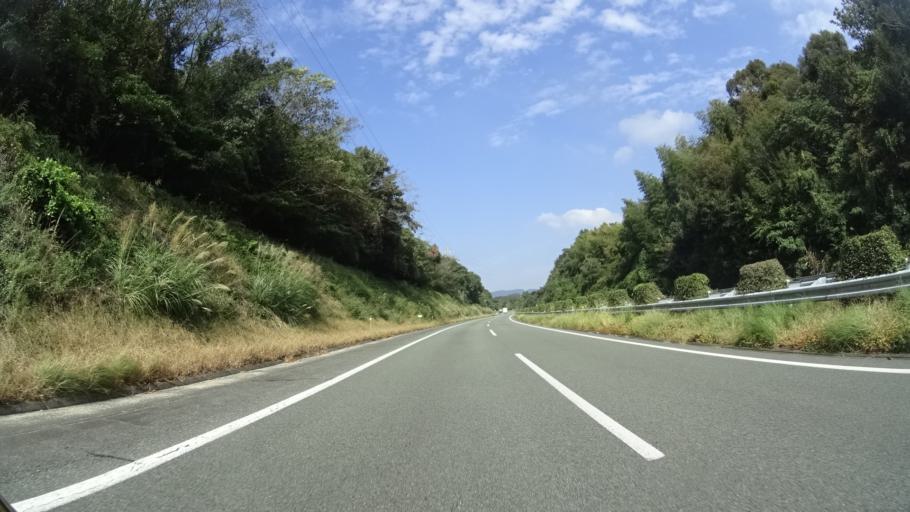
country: JP
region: Kumamoto
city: Matsubase
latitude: 32.6315
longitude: 130.7102
